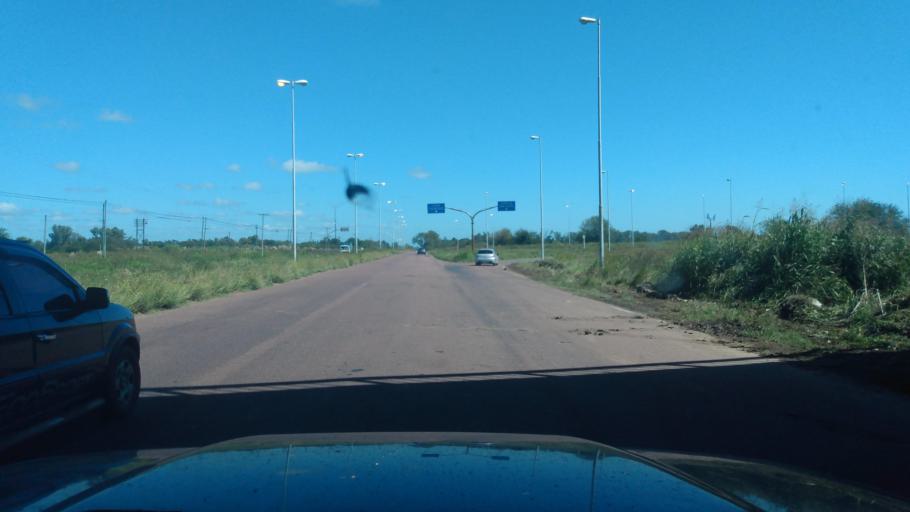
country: AR
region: Buenos Aires
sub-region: Partido de Lujan
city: Lujan
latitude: -34.5886
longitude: -59.0378
